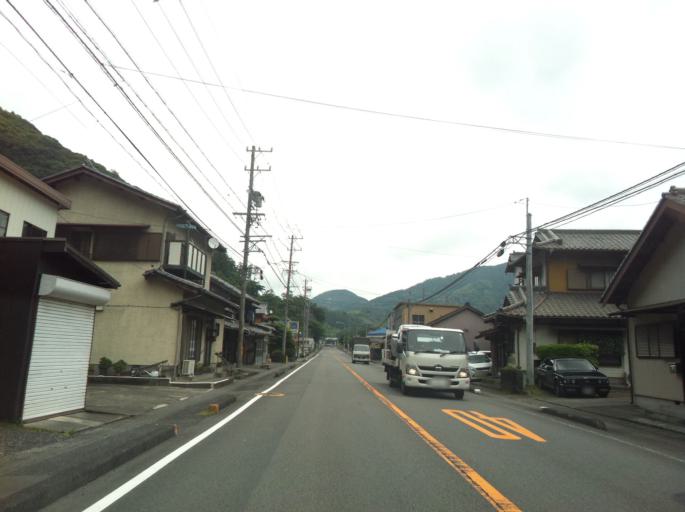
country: JP
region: Shizuoka
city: Fujieda
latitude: 34.9211
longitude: 138.2842
